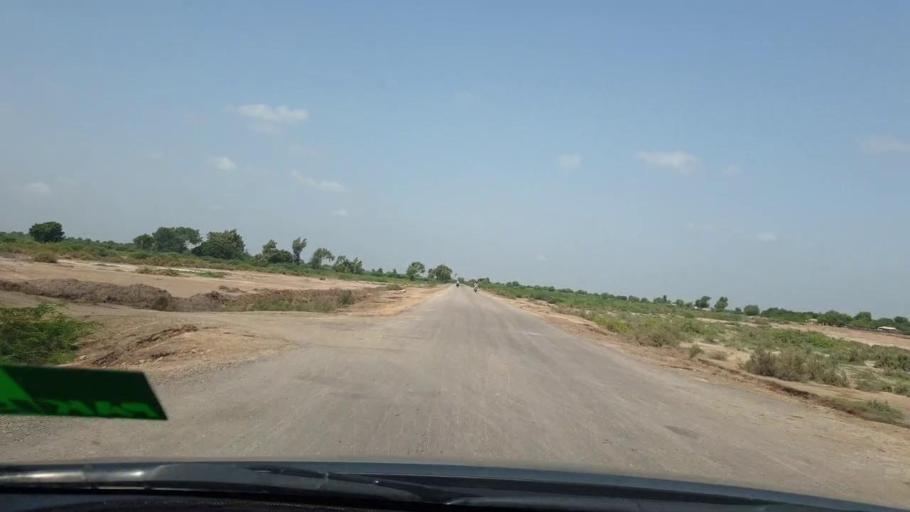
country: PK
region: Sindh
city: Digri
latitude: 24.9921
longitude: 69.1253
